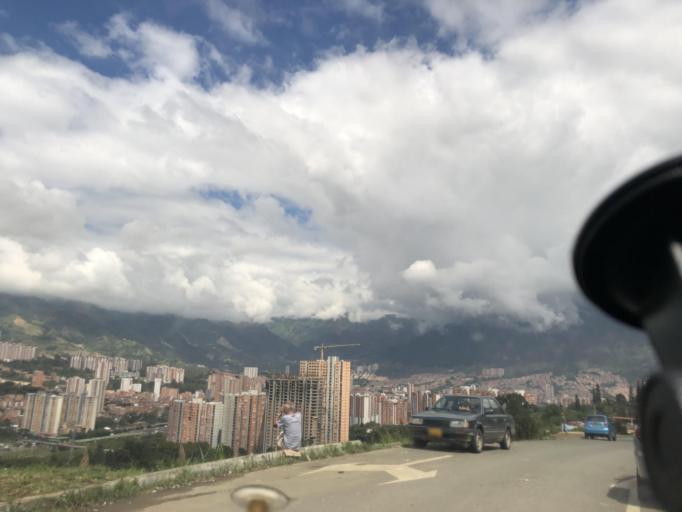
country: CO
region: Antioquia
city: Bello
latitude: 6.3100
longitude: -75.5489
